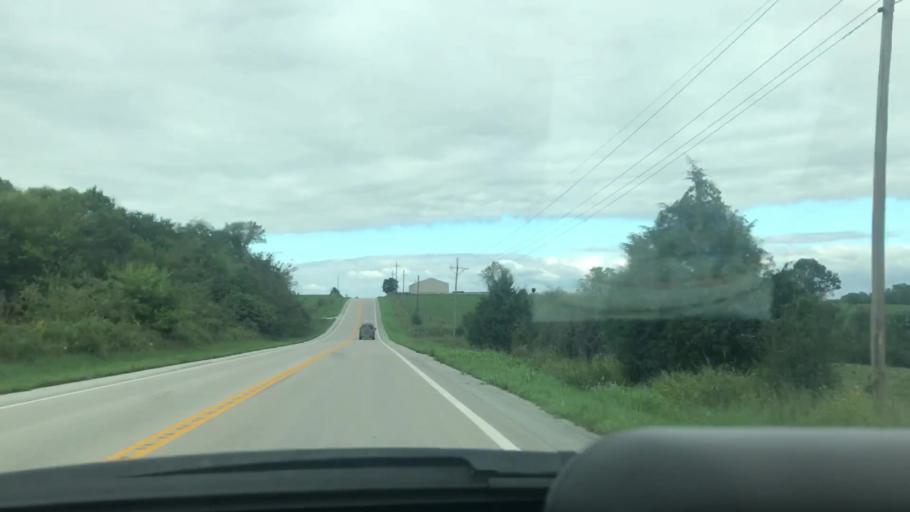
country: US
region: Missouri
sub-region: Hickory County
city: Hermitage
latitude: 37.8808
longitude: -93.1802
